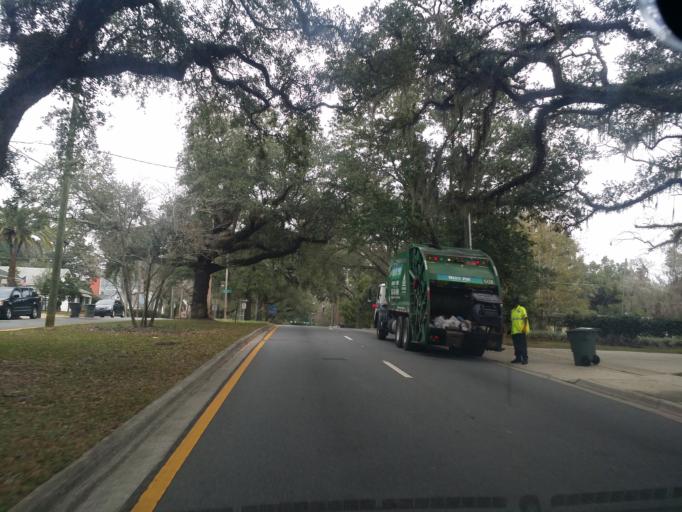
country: US
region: Florida
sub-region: Leon County
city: Tallahassee
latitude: 30.4558
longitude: -84.2831
